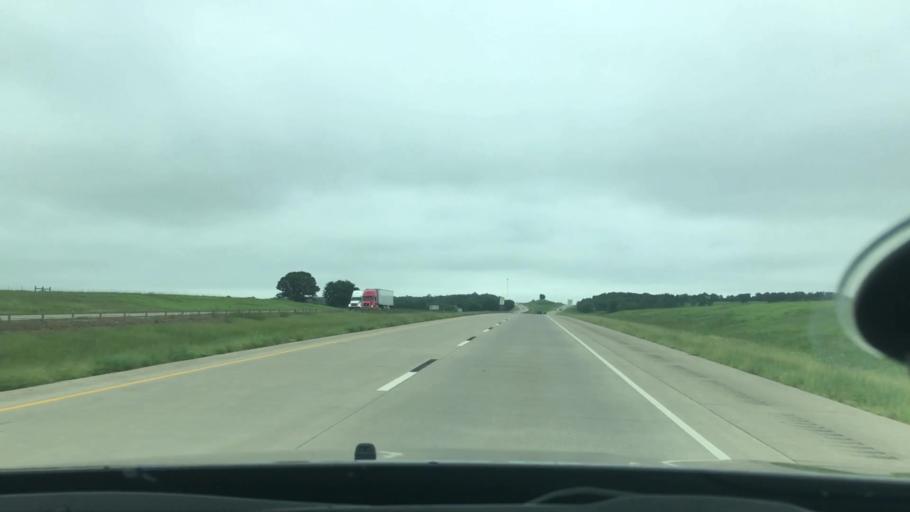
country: US
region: Oklahoma
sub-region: McIntosh County
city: Checotah
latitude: 35.4573
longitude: -95.4425
